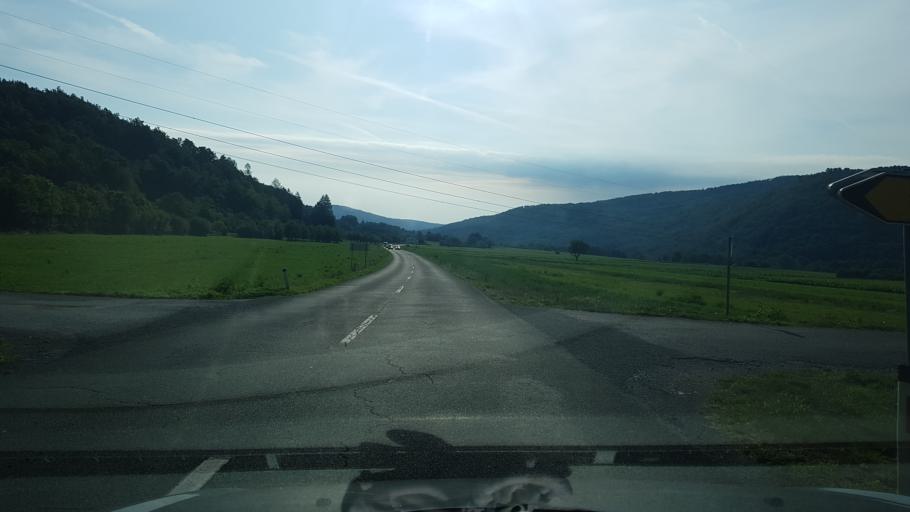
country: SI
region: Divaca
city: Divaca
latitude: 45.6555
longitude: 14.0340
